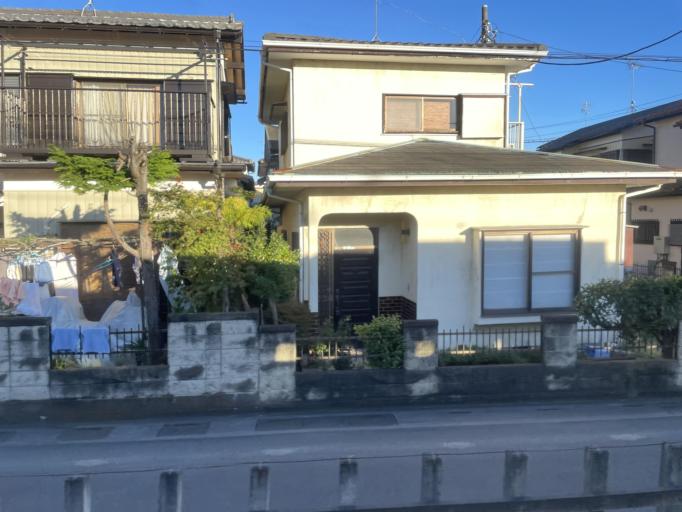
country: JP
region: Saitama
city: Satte
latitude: 36.0867
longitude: 139.7167
